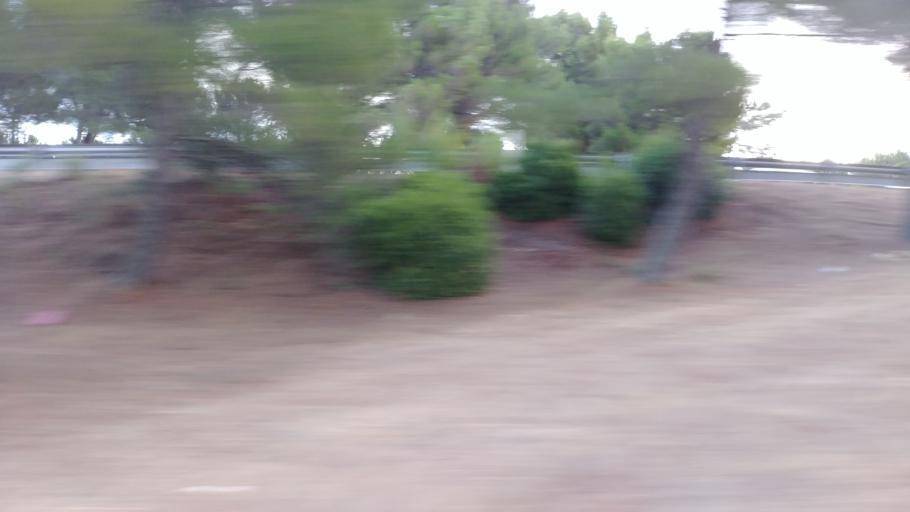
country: FR
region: Provence-Alpes-Cote d'Azur
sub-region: Departement des Bouches-du-Rhone
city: Venelles
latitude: 43.5728
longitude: 5.4669
